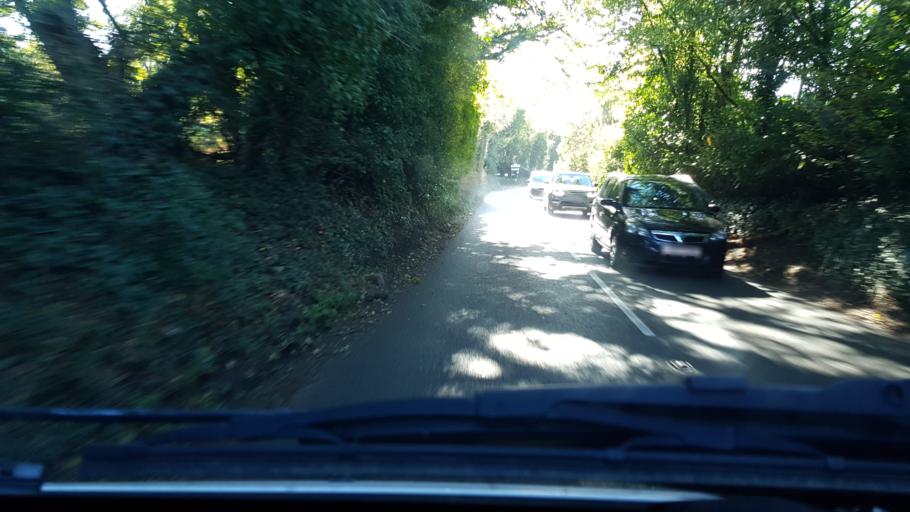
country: GB
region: England
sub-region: Surrey
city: Chilworth
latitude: 51.1917
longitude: -0.5311
